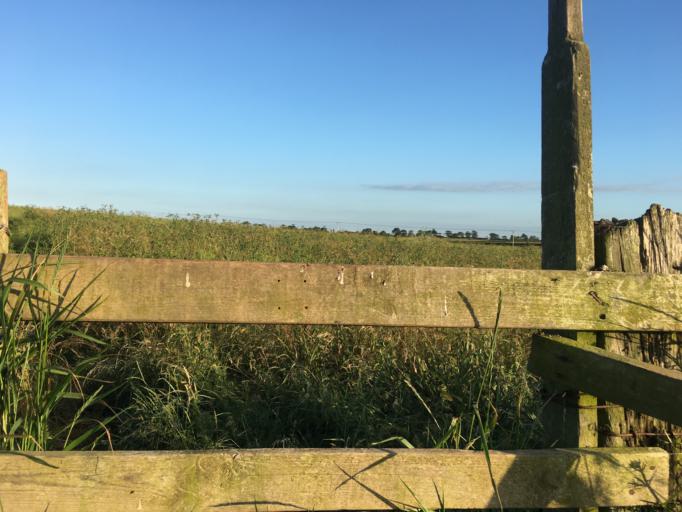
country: GB
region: England
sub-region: Northumberland
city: North Sunderland
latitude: 55.5843
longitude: -1.6750
